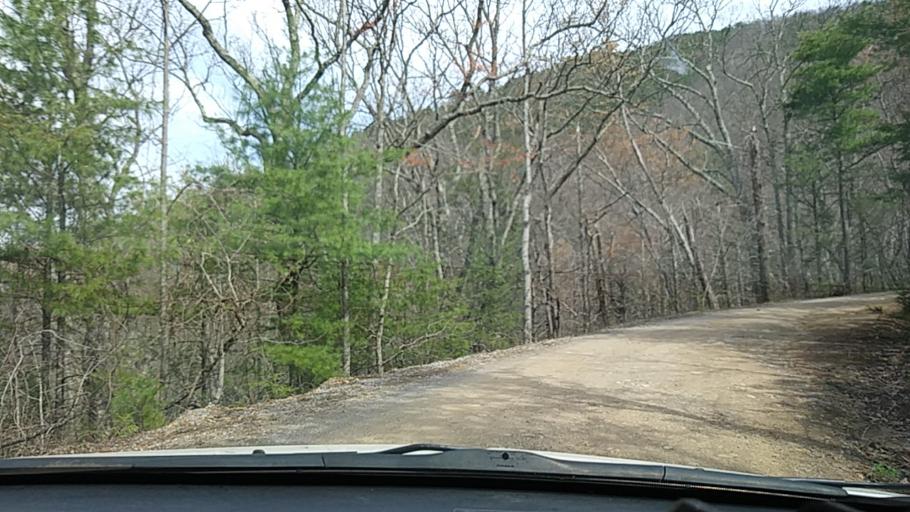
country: US
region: Tennessee
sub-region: Greene County
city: Tusculum
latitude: 36.0872
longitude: -82.6907
